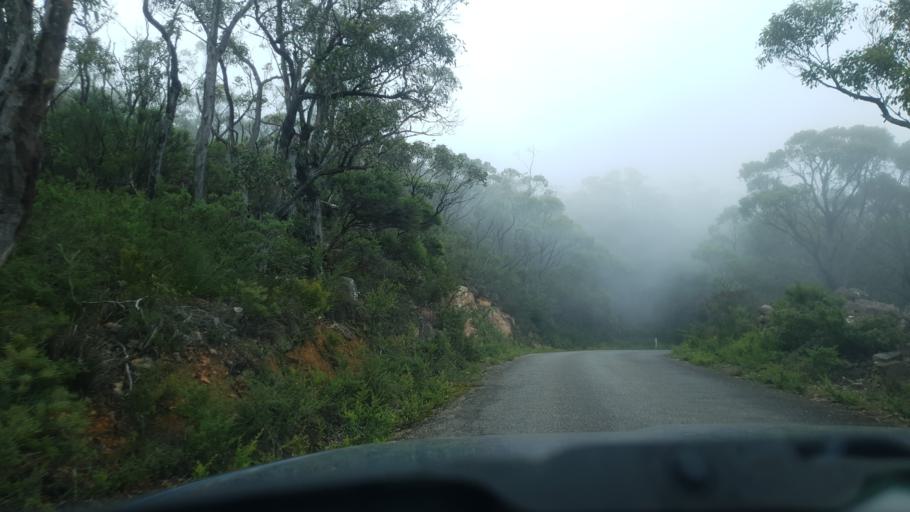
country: AU
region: Victoria
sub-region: Northern Grampians
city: Stawell
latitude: -37.2777
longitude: 142.5852
